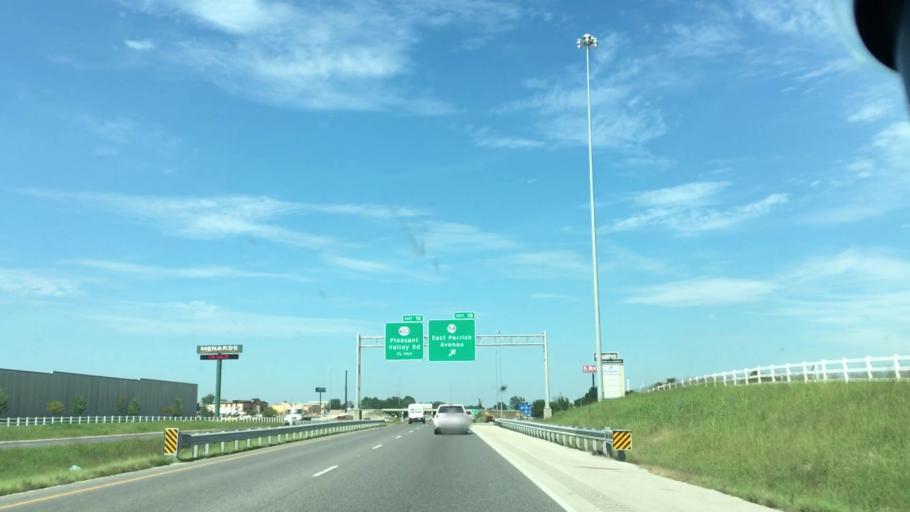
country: US
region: Kentucky
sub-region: Daviess County
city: Owensboro
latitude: 37.7527
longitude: -87.0712
